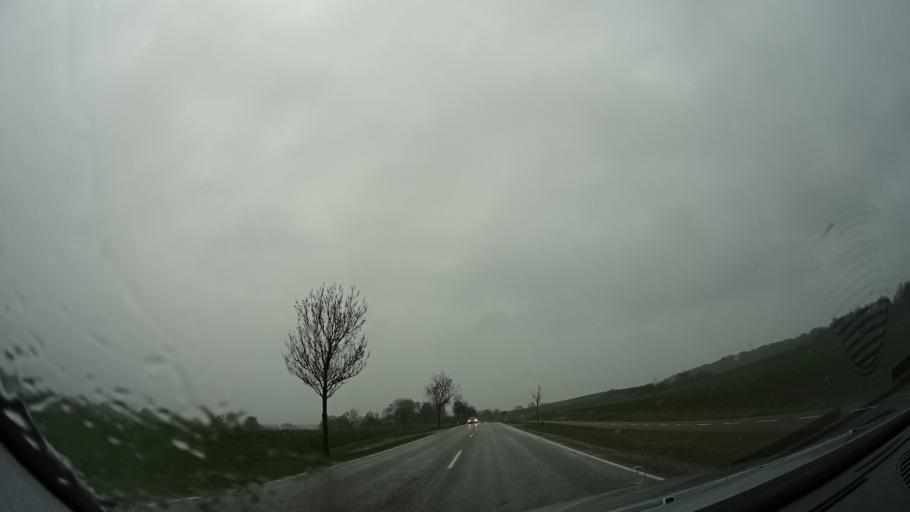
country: DK
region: Zealand
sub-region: Lejre Kommune
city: Ejby
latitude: 55.6749
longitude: 11.8336
